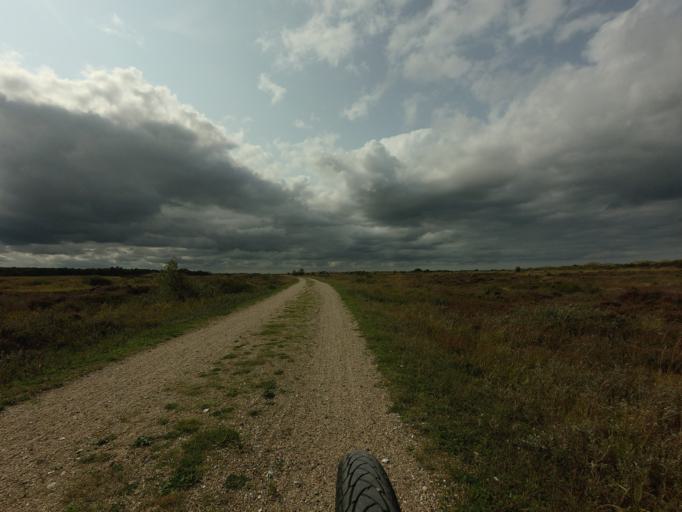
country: DK
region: North Denmark
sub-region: Frederikshavn Kommune
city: Strandby
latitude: 57.6417
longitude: 10.4032
